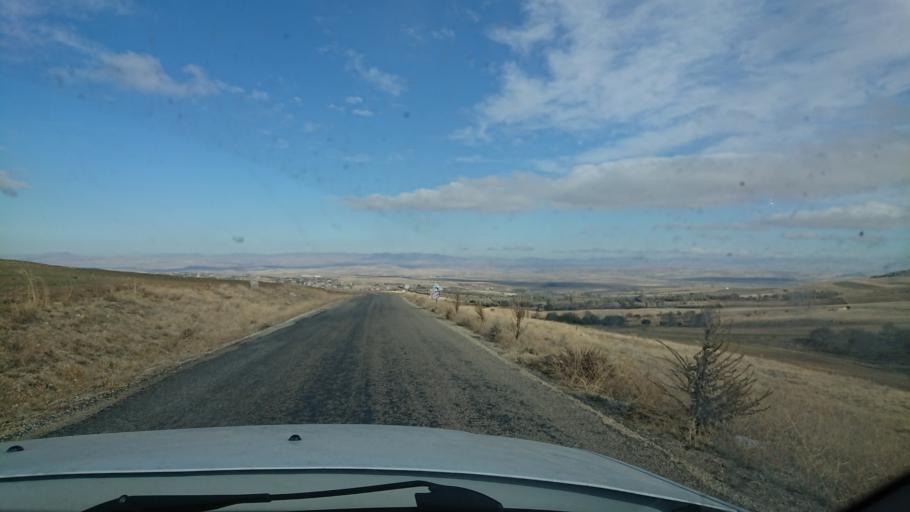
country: TR
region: Aksaray
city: Agacoren
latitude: 38.8419
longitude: 33.9527
